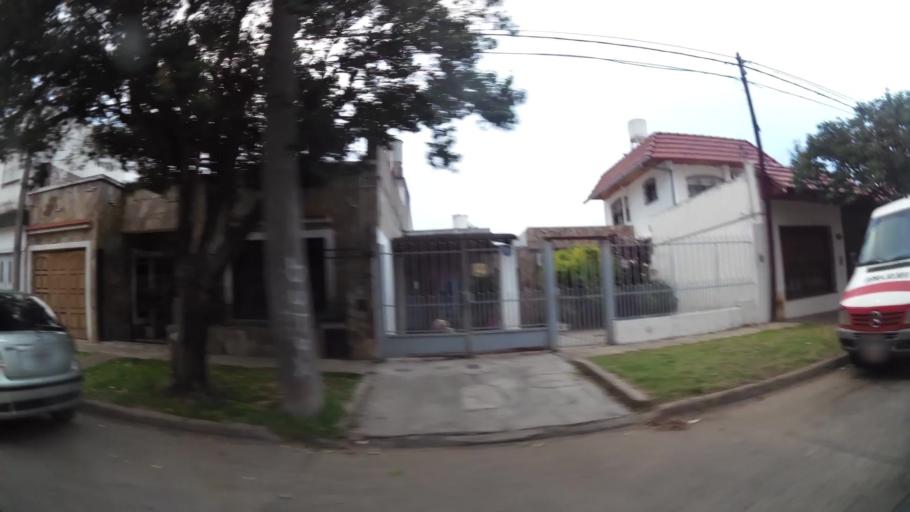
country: AR
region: Santa Fe
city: Granadero Baigorria
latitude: -32.8824
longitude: -60.6985
